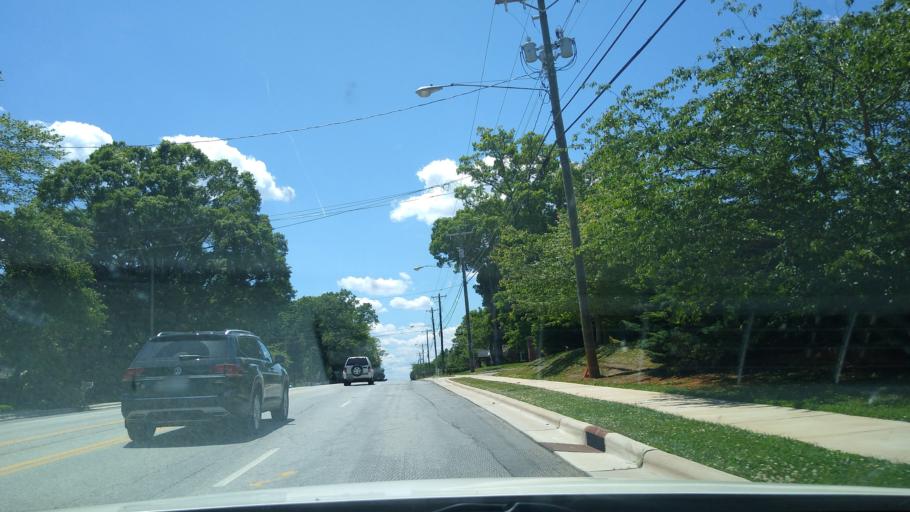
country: US
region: North Carolina
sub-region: Guilford County
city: Jamestown
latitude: 36.0813
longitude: -79.8937
